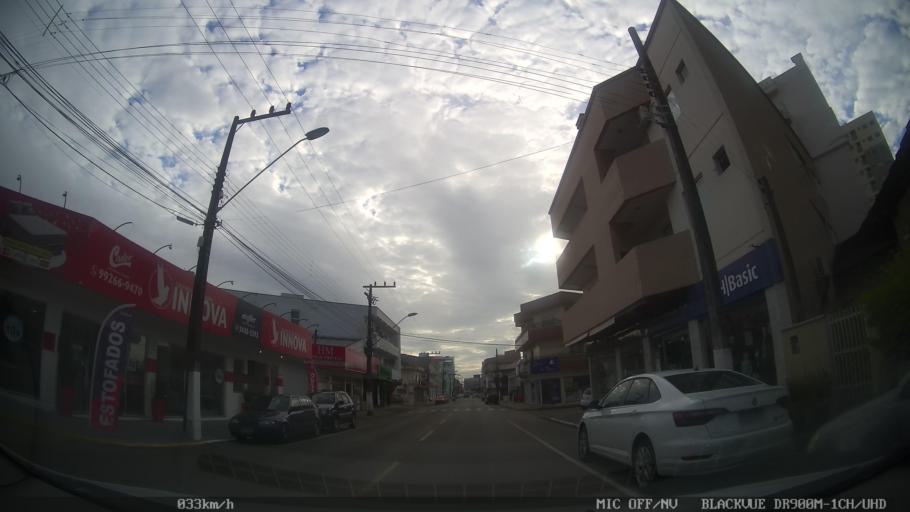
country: BR
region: Santa Catarina
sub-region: Barra Velha
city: Barra Velha
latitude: -26.6445
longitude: -48.6862
